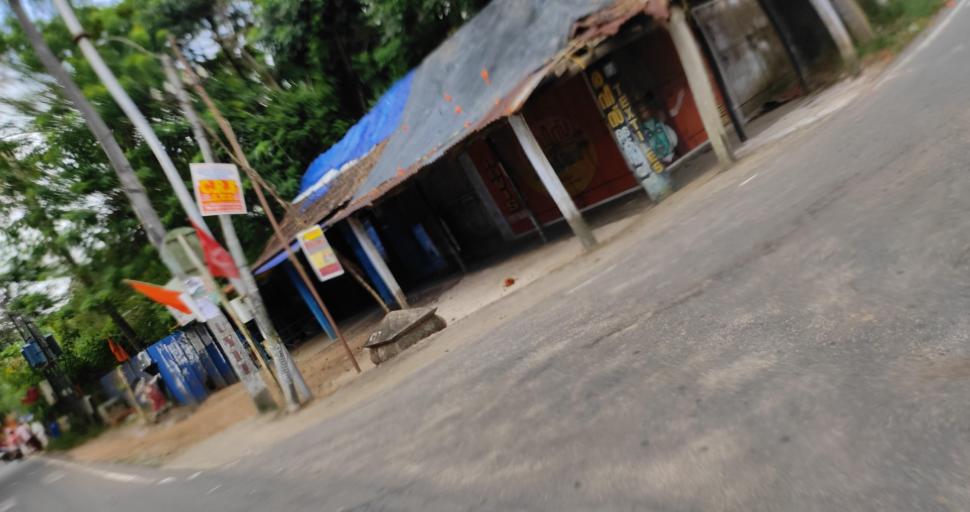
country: IN
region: Kerala
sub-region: Alappuzha
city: Shertallai
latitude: 9.6534
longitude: 76.3178
